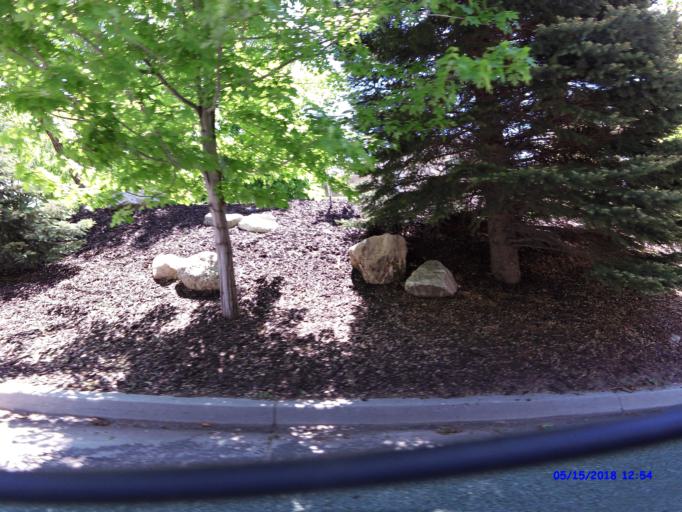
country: US
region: Utah
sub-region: Weber County
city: Uintah
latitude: 41.1592
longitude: -111.9210
